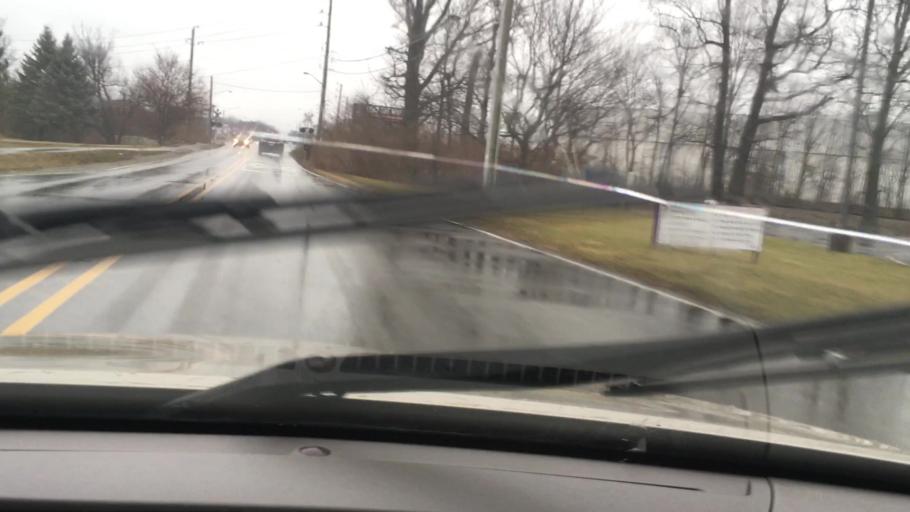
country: US
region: Indiana
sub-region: Marion County
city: Lawrence
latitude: 39.8833
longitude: -86.0746
